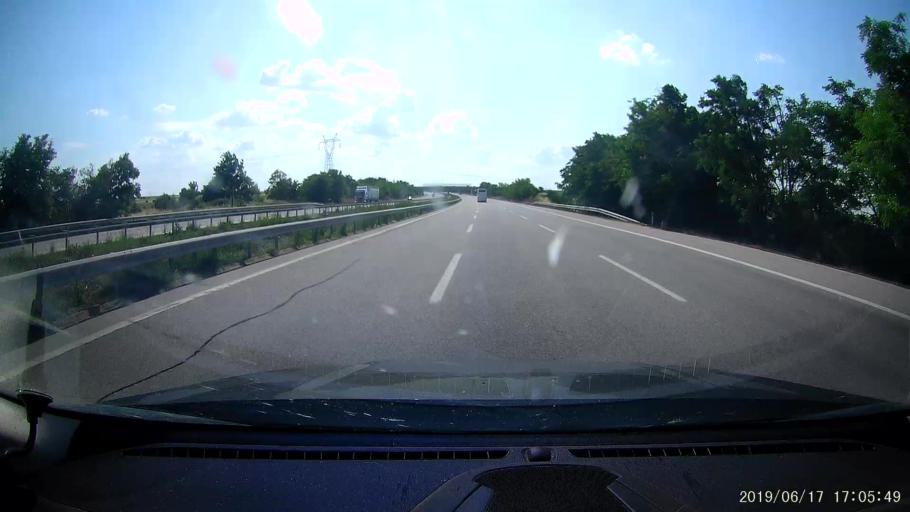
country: TR
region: Edirne
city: Edirne
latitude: 41.6619
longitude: 26.6883
